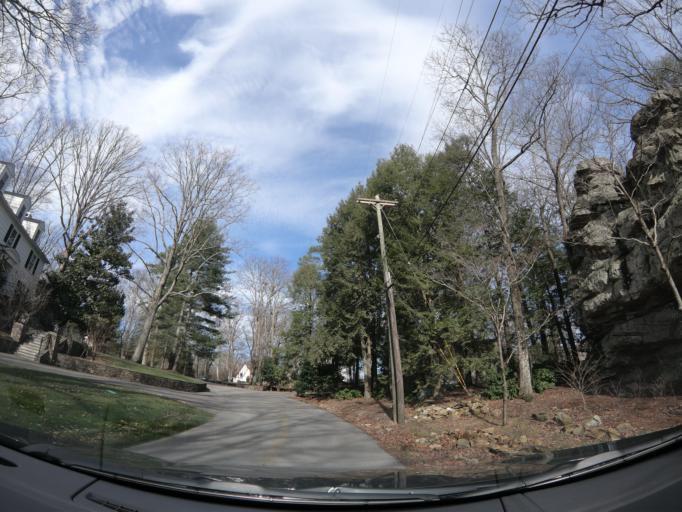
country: US
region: Georgia
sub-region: Walker County
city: Lookout Mountain
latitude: 34.9815
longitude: -85.3492
